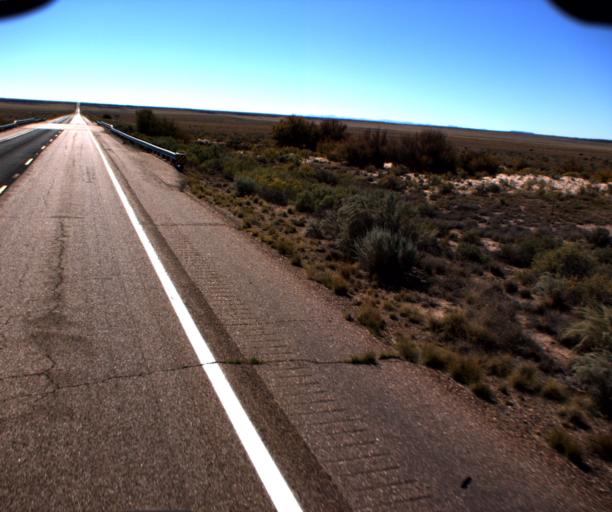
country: US
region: Arizona
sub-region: Navajo County
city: Snowflake
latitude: 34.7451
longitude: -109.7965
